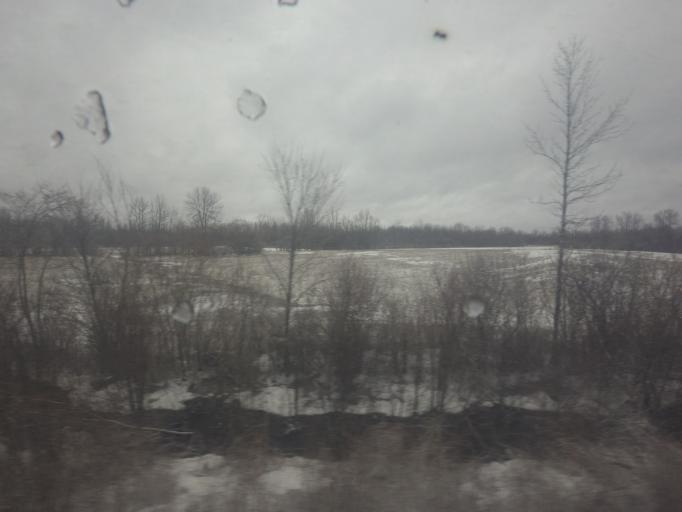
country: CA
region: Ontario
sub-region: Lanark County
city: Smiths Falls
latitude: 44.9297
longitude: -76.0269
